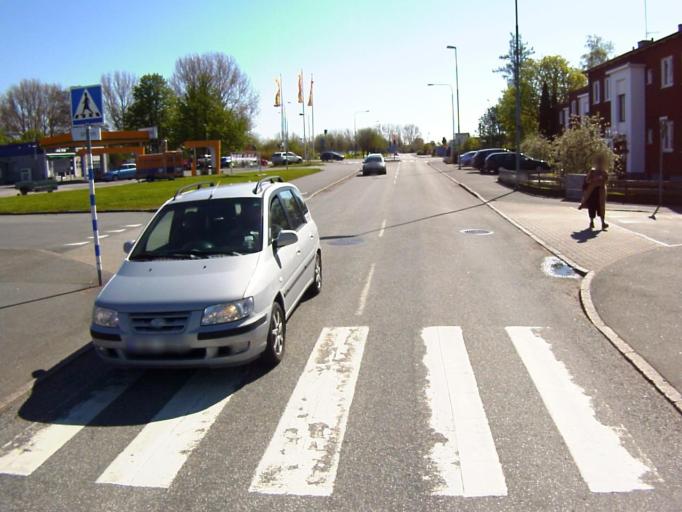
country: SE
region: Skane
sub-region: Kristianstads Kommun
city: Kristianstad
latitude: 56.0492
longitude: 14.1570
